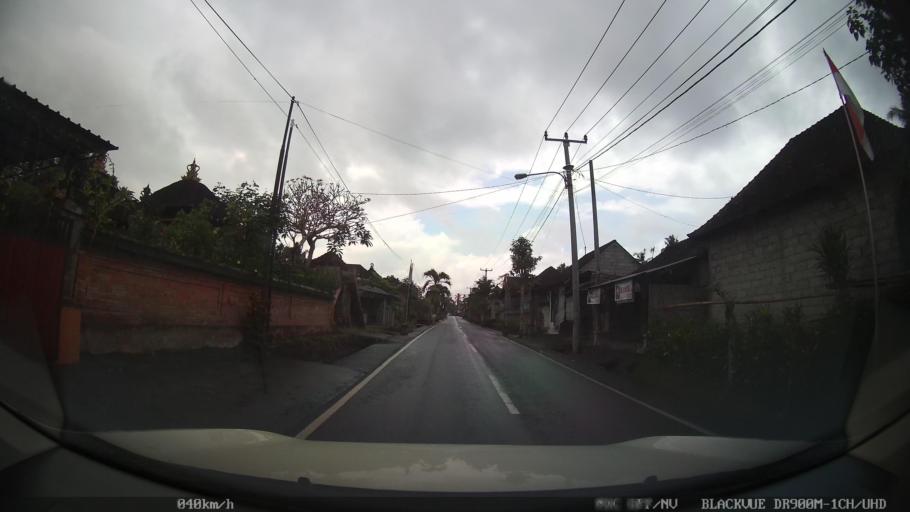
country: ID
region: Bali
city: Banjar Teguan
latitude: -8.5204
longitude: 115.2284
